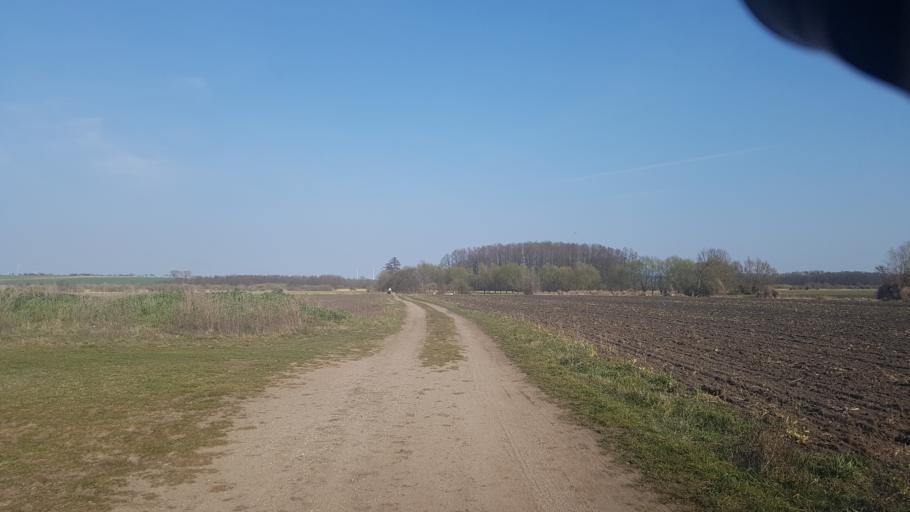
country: DE
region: Brandenburg
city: Prenzlau
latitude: 53.2246
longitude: 13.8491
